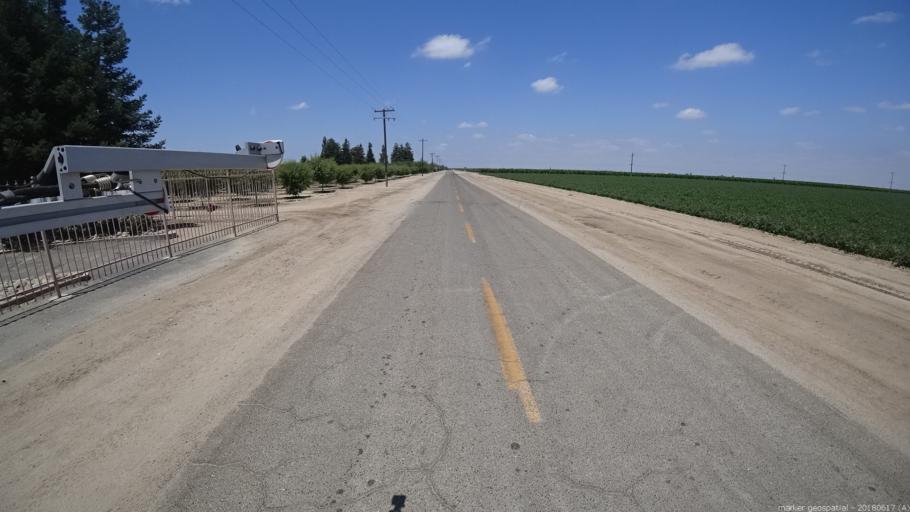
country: US
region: California
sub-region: Fresno County
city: Kerman
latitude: 36.8208
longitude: -120.1510
